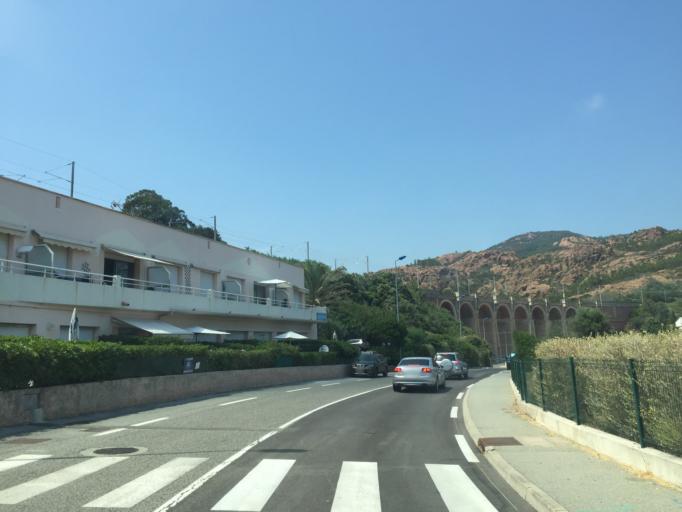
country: FR
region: Provence-Alpes-Cote d'Azur
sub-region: Departement des Alpes-Maritimes
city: Theoule-sur-Mer
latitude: 43.4355
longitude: 6.8927
